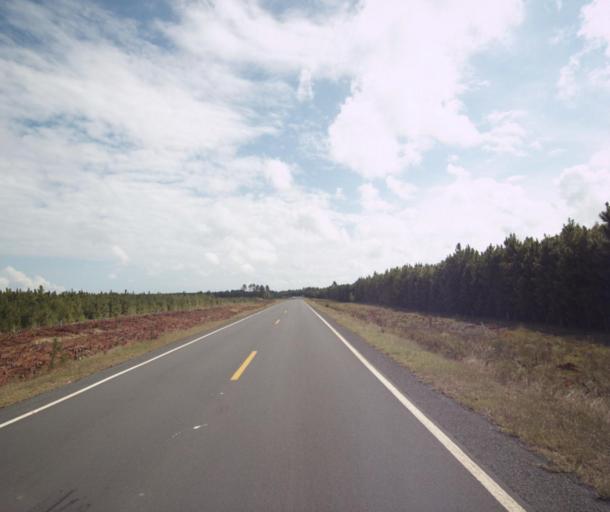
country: BR
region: Rio Grande do Sul
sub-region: Sao Lourenco Do Sul
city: Sao Lourenco do Sul
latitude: -31.4612
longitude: -51.2279
